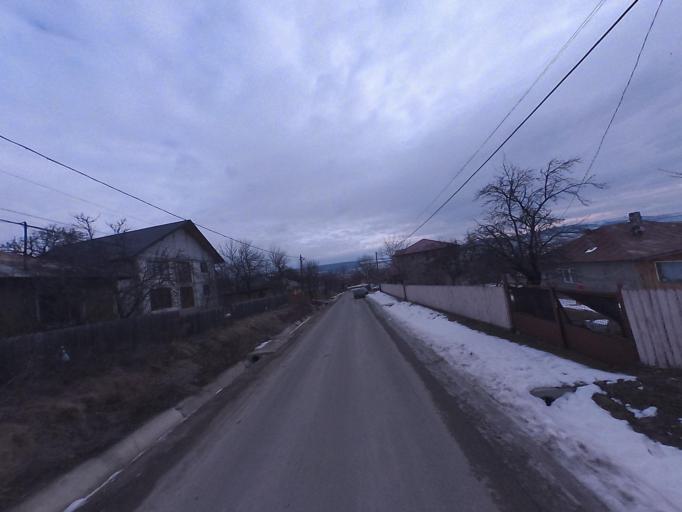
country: RO
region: Iasi
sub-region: Comuna Tibanesti
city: Glodenii Gandului
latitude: 46.9787
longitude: 27.3023
